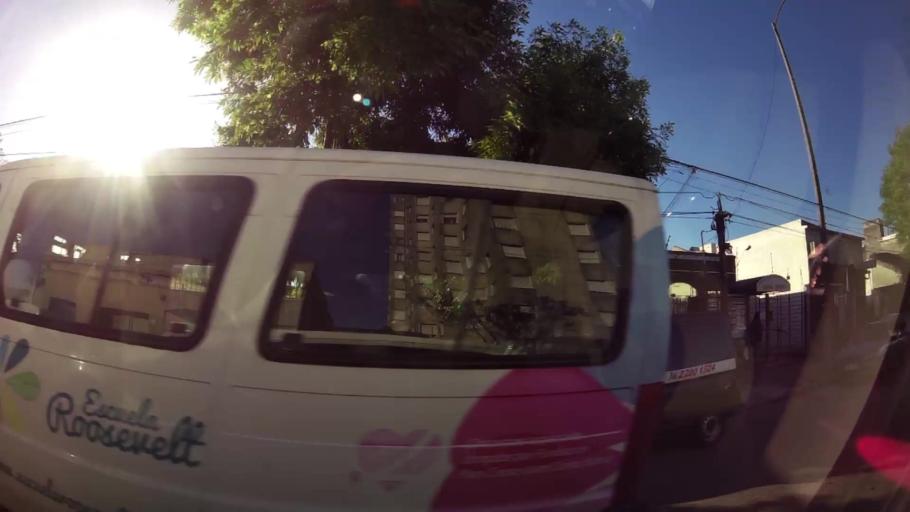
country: UY
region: Canelones
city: La Paz
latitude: -34.8331
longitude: -56.2156
